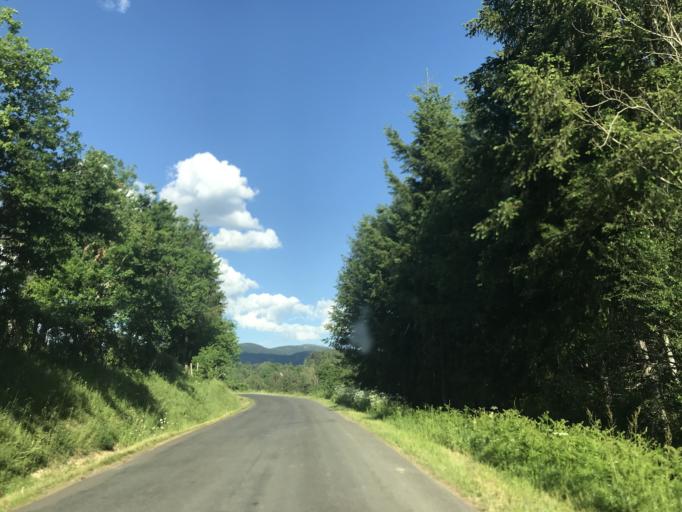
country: FR
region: Auvergne
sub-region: Departement du Puy-de-Dome
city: Job
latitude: 45.6546
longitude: 3.6675
